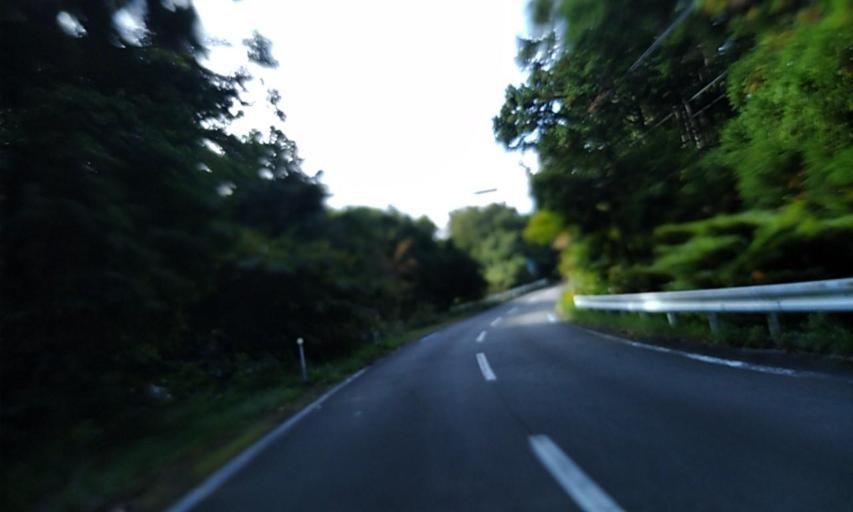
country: JP
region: Wakayama
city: Shingu
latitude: 33.4693
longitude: 135.8381
